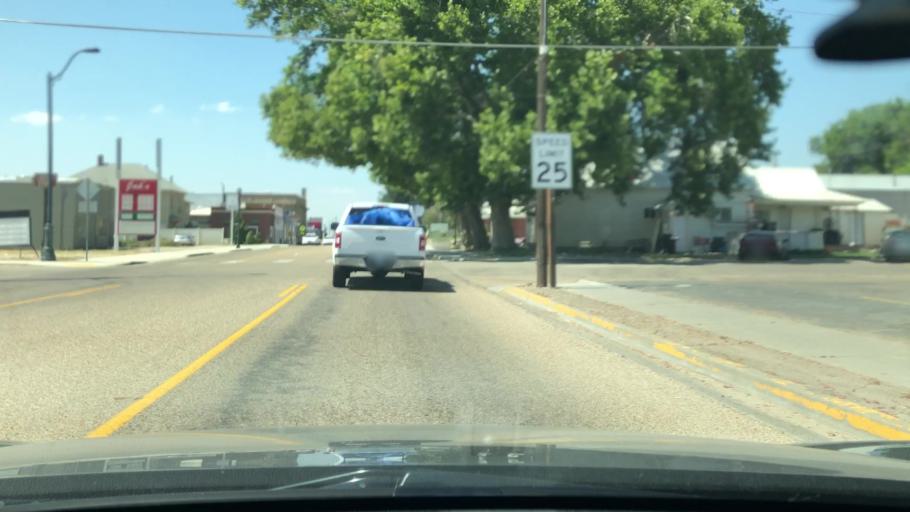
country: US
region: Idaho
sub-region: Canyon County
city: Parma
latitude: 43.7848
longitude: -116.9426
